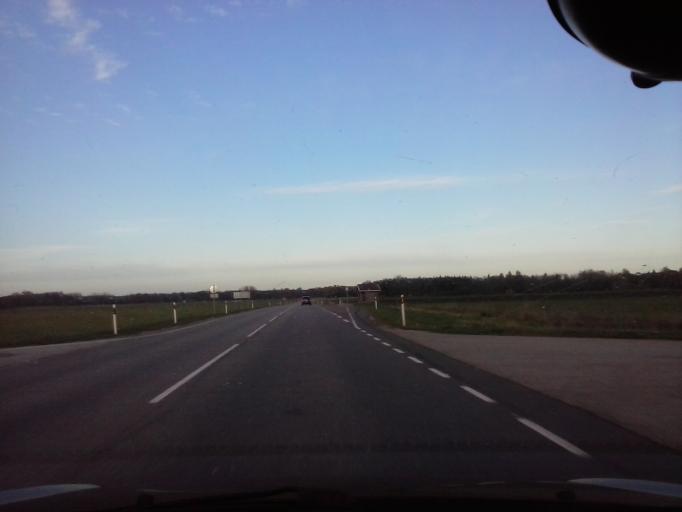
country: EE
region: Laeaene
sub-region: Ridala Parish
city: Uuemoisa
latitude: 58.9687
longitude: 23.8370
